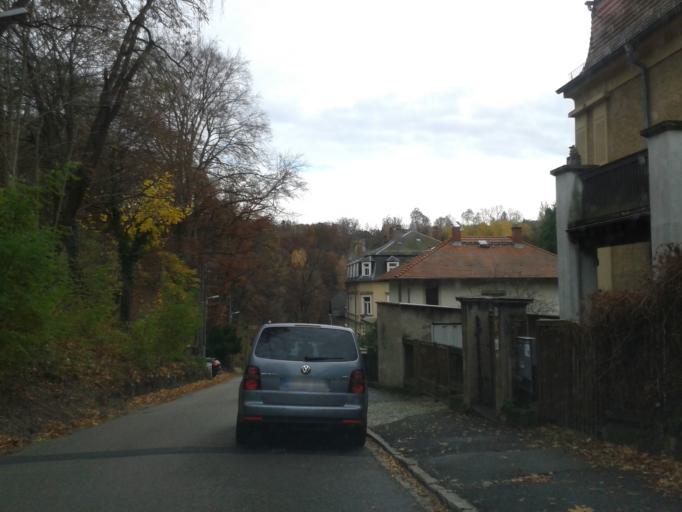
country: DE
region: Saxony
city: Albertstadt
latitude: 51.0599
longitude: 13.8265
